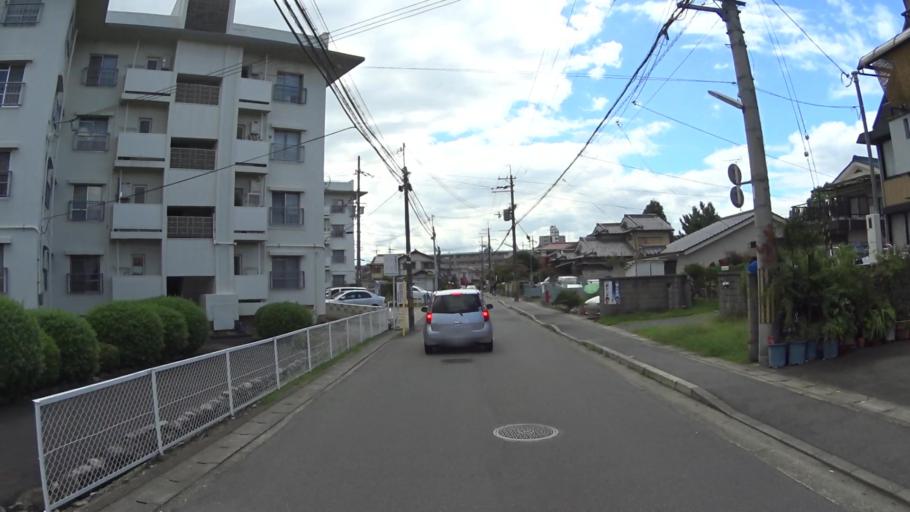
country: JP
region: Kyoto
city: Yawata
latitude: 34.9085
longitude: 135.7228
